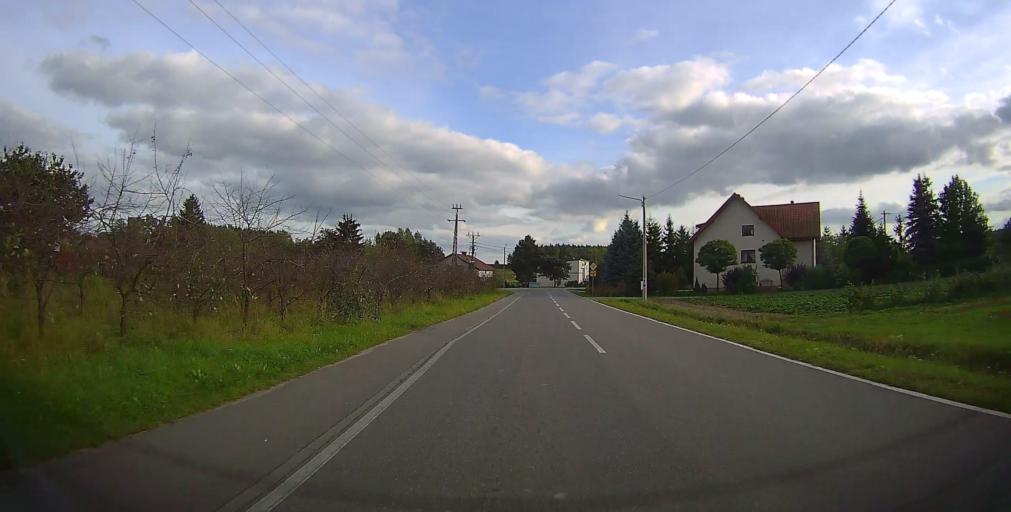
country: PL
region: Masovian Voivodeship
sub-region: Powiat grojecki
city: Jasieniec
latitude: 51.7561
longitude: 20.9562
